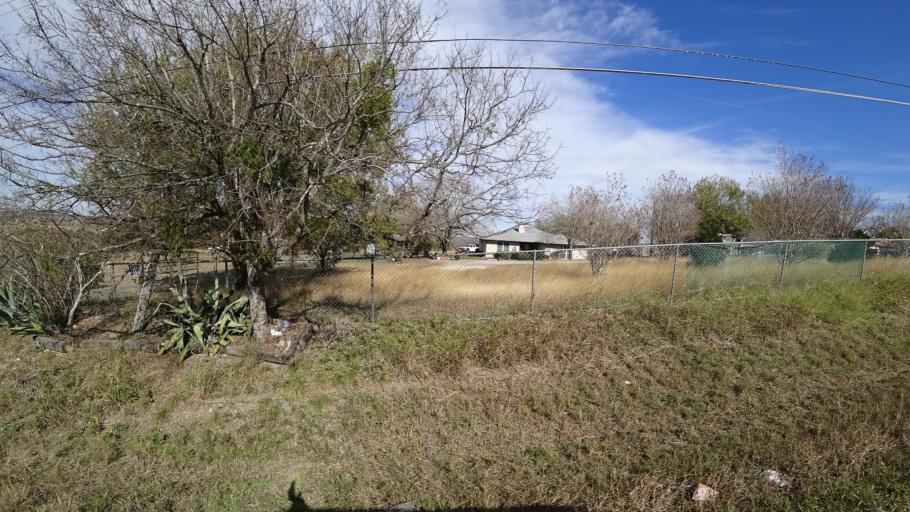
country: US
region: Texas
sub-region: Travis County
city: Onion Creek
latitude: 30.1165
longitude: -97.7055
